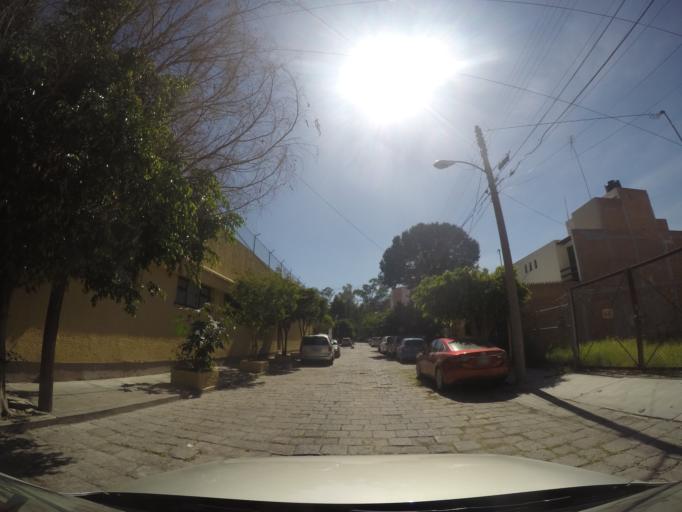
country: MX
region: San Luis Potosi
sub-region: San Luis Potosi
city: San Luis Potosi
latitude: 22.1499
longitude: -101.0138
